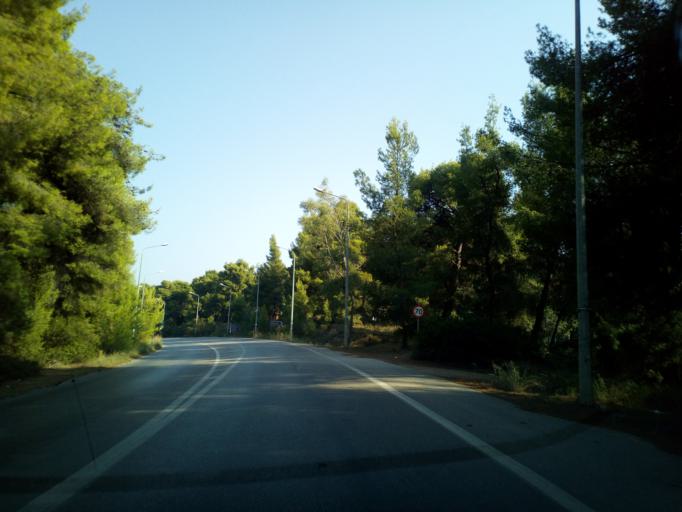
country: GR
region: Central Macedonia
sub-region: Nomos Chalkidikis
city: Nikiti
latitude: 40.2340
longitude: 23.6014
